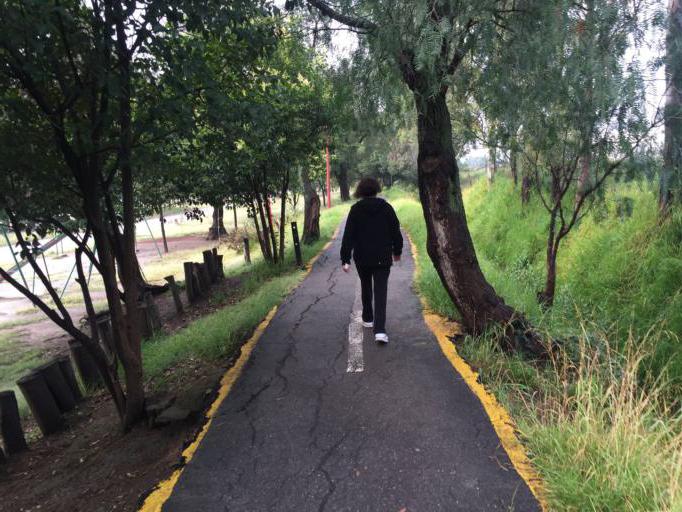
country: MX
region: Mexico
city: Cuautitlan Izcalli
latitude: 19.6535
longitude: -99.2233
